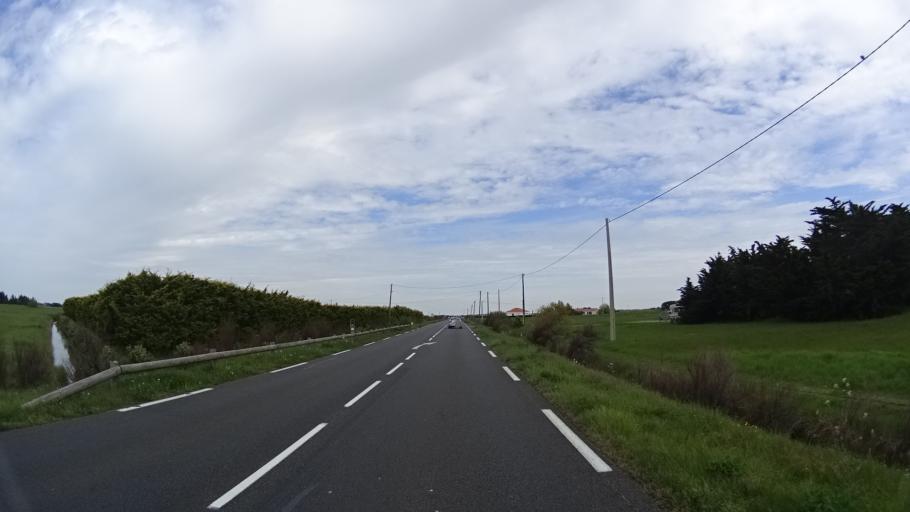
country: FR
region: Pays de la Loire
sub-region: Departement de la Vendee
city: Bouin
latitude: 46.9474
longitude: -2.0249
